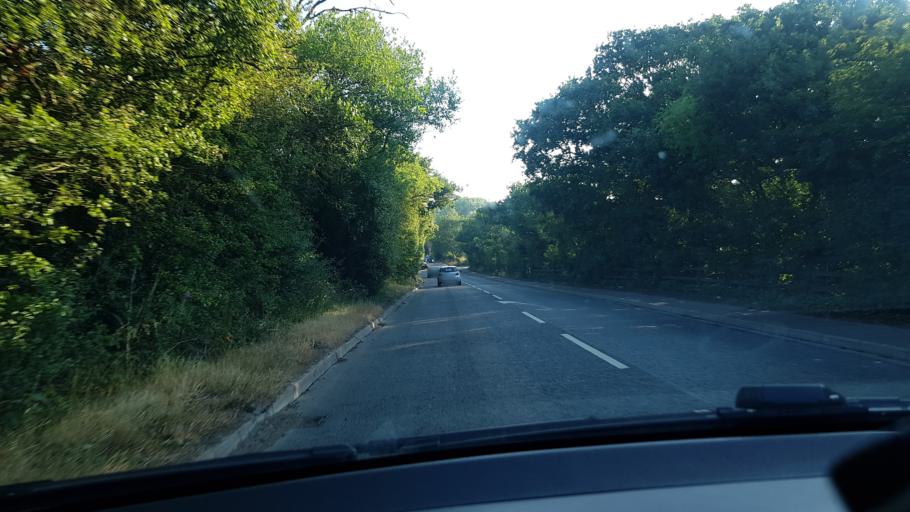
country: GB
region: England
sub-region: Derbyshire
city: Ilkeston
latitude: 52.9491
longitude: -1.3083
